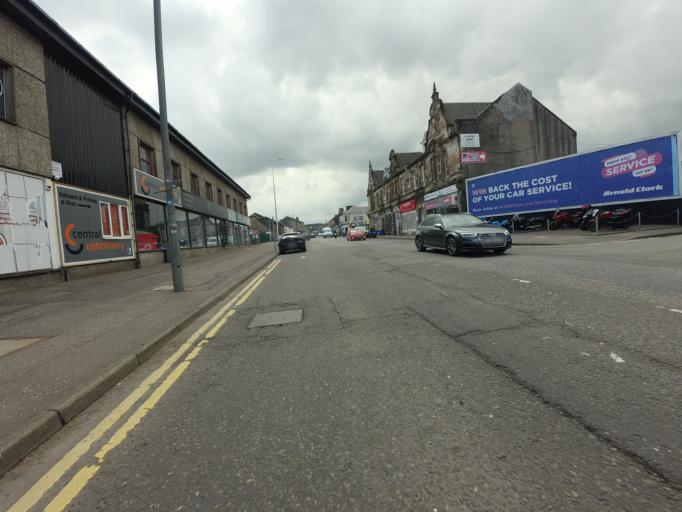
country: GB
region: Scotland
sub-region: Falkirk
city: Falkirk
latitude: 56.0088
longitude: -3.7847
